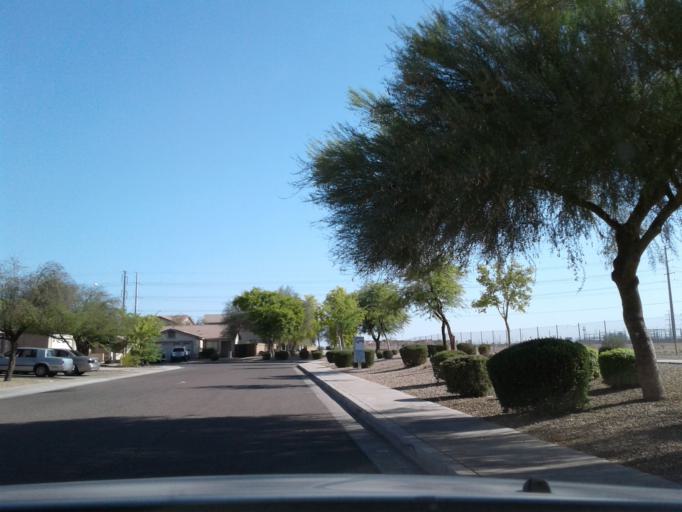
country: US
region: Arizona
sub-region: Maricopa County
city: Laveen
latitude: 33.4135
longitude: -112.1925
